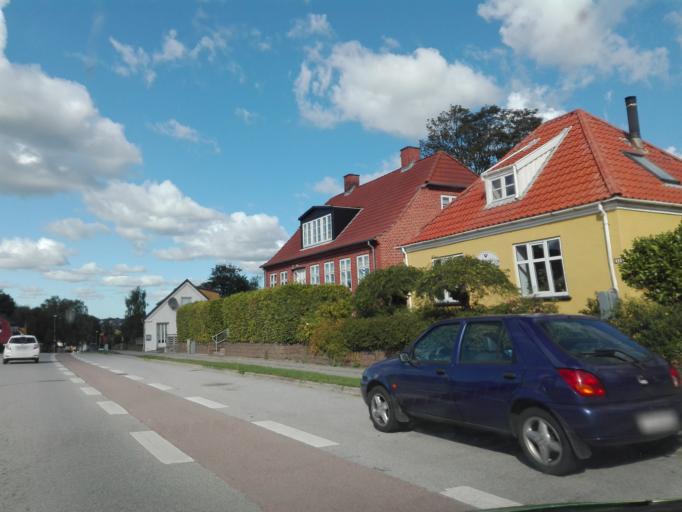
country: DK
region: North Denmark
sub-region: Mariagerfjord Kommune
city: Hobro
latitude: 56.6312
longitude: 9.8010
